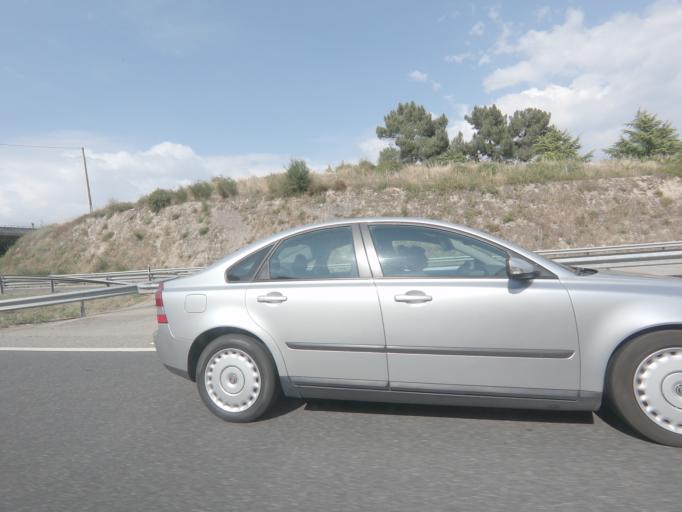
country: ES
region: Galicia
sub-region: Provincia de Ourense
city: Ourense
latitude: 42.3144
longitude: -7.8860
